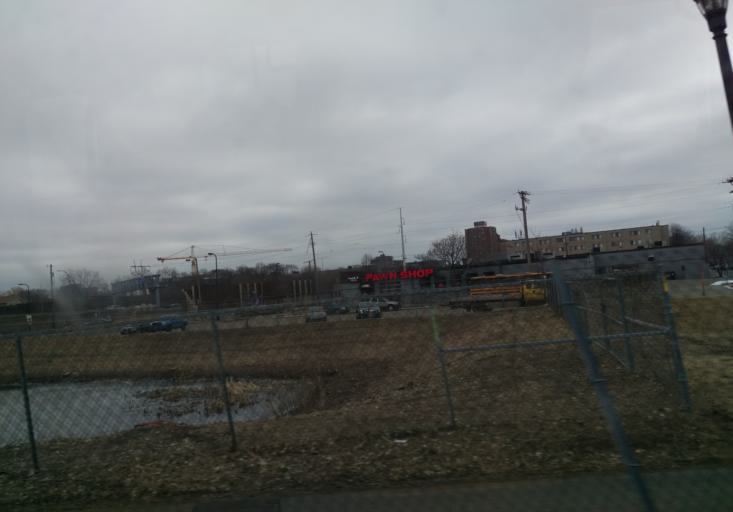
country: US
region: Minnesota
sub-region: Hennepin County
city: Minneapolis
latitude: 44.9641
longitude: -93.2480
